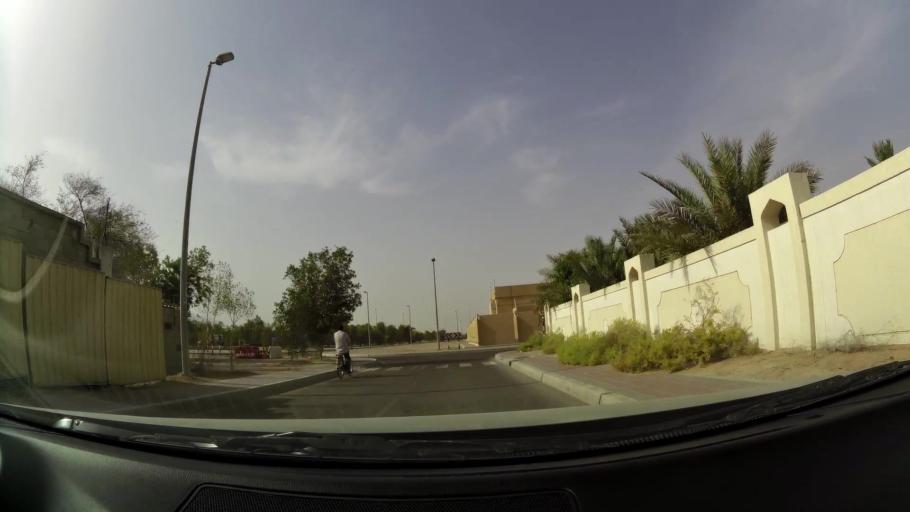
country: AE
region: Abu Dhabi
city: Al Ain
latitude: 24.1339
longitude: 55.7076
